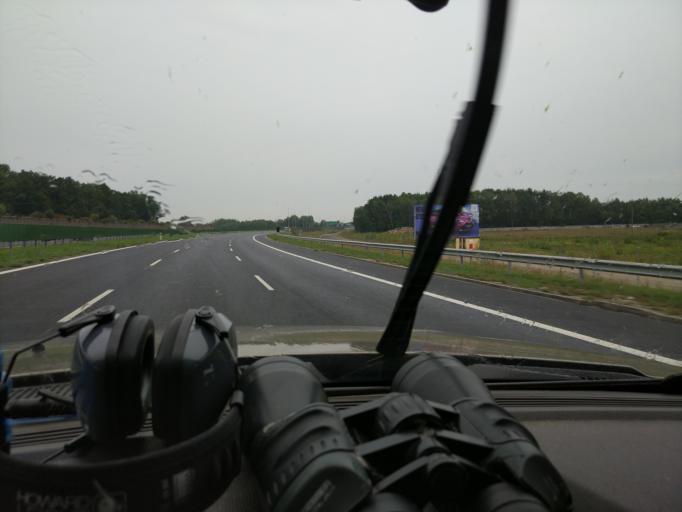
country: PL
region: Masovian Voivodeship
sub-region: Powiat wolominski
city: Slupno
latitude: 52.3465
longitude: 21.1569
